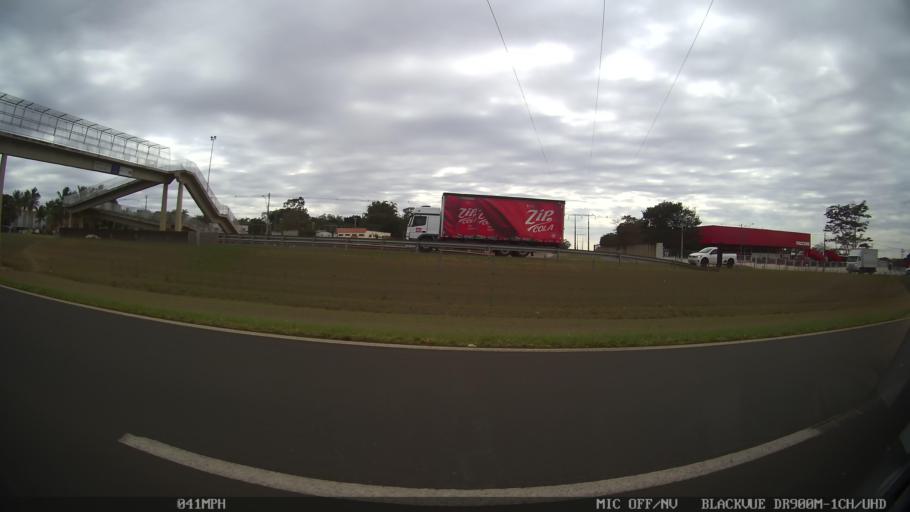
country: BR
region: Sao Paulo
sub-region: Bady Bassitt
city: Bady Bassitt
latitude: -20.8063
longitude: -49.5171
